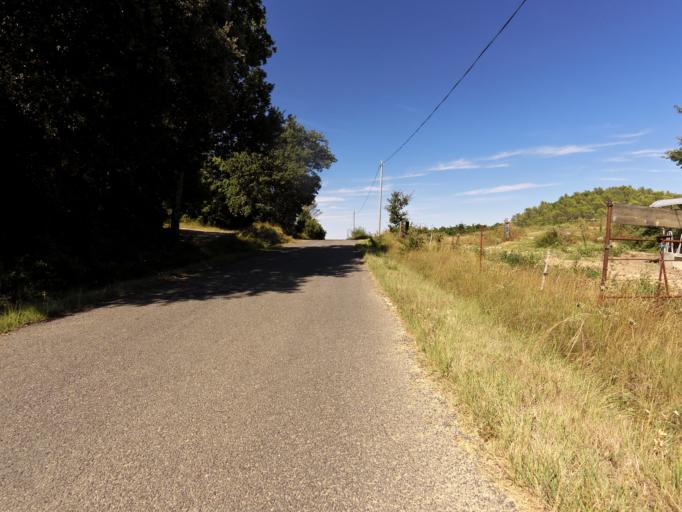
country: FR
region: Languedoc-Roussillon
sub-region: Departement du Gard
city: Quissac
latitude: 43.9335
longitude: 4.0488
